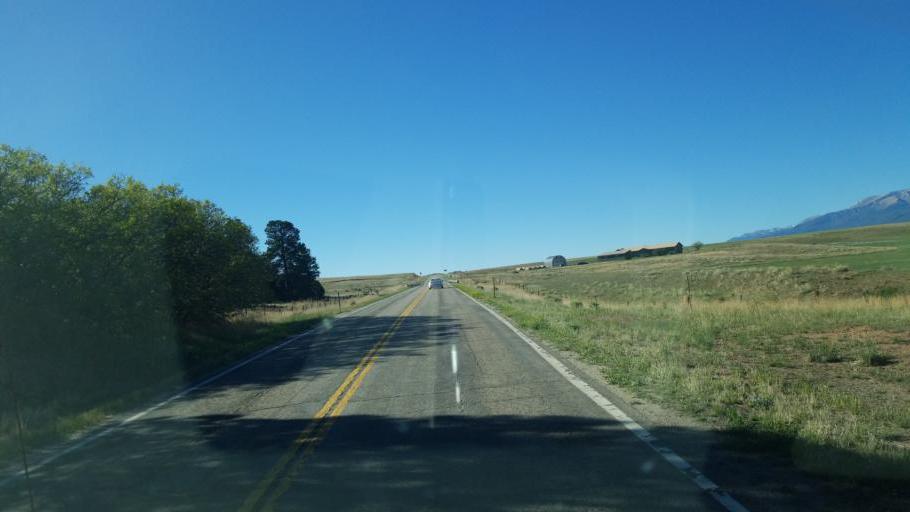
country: US
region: Colorado
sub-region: Custer County
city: Westcliffe
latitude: 38.2164
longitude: -105.5501
